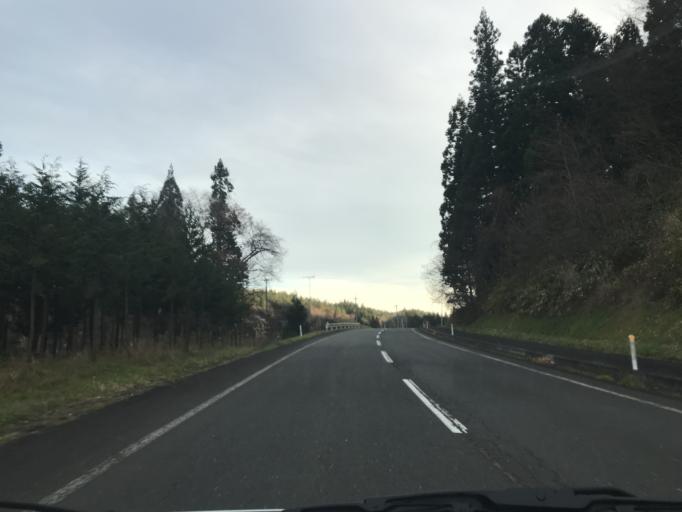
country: JP
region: Iwate
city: Ichinoseki
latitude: 38.9933
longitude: 141.0657
